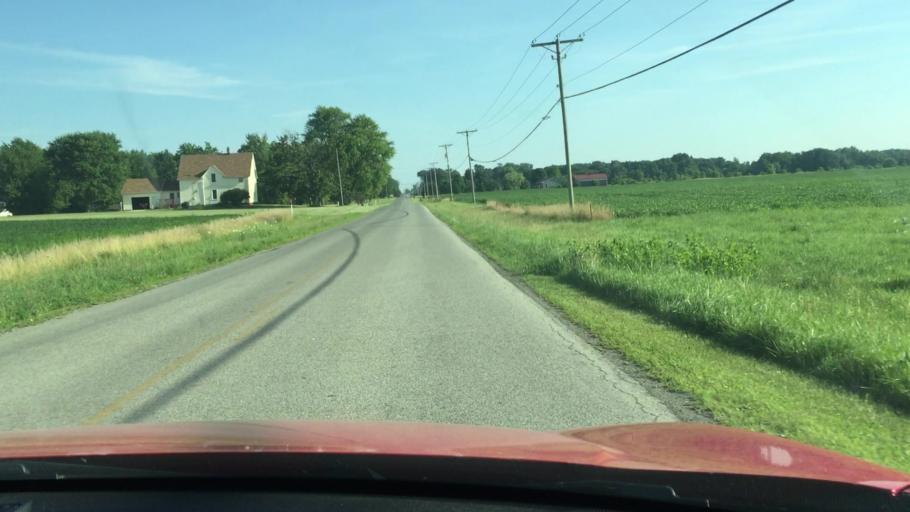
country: US
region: Ohio
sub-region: Hardin County
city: Ada
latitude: 40.7422
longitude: -83.8424
